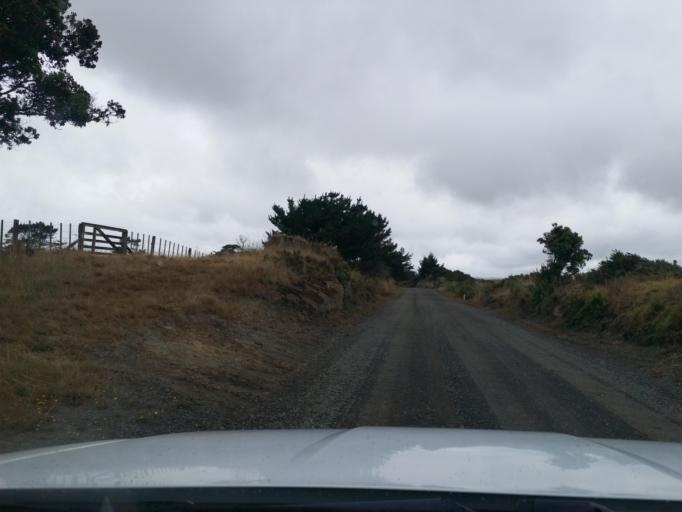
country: NZ
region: Northland
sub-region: Kaipara District
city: Dargaville
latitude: -36.0362
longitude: 173.8576
